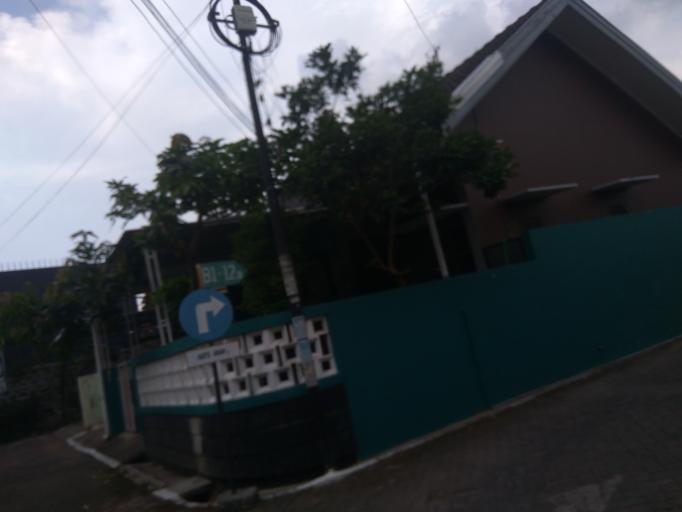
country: ID
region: Central Java
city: Semarang
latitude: -7.0654
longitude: 110.4447
